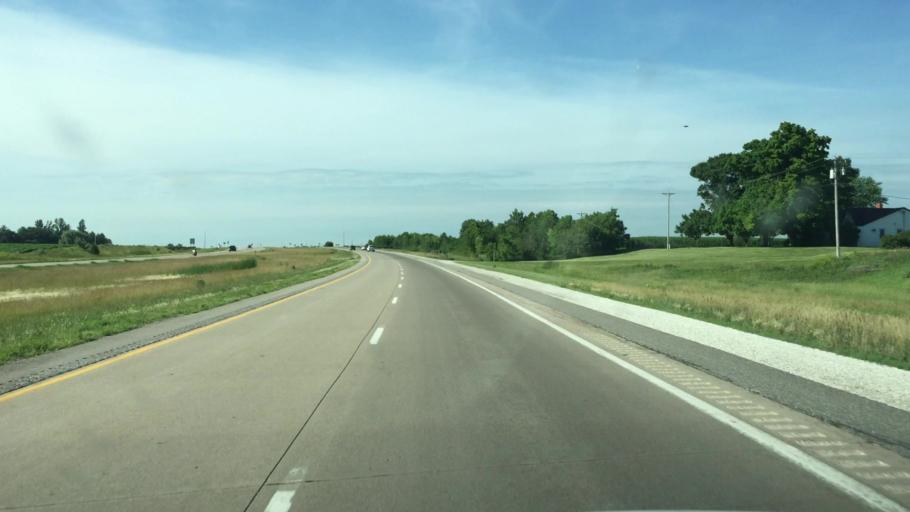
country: US
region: Iowa
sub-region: Henry County
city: Winfield
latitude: 41.1686
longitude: -91.5420
